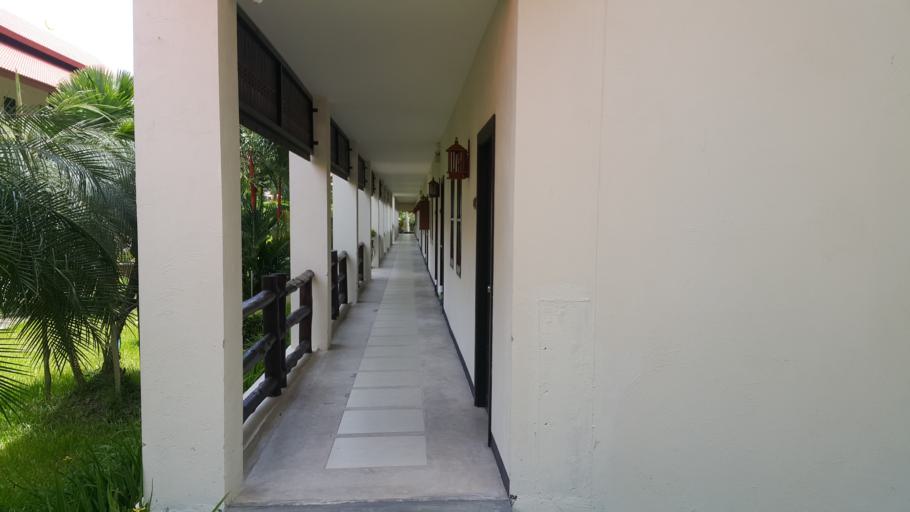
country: TH
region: Chiang Mai
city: San Sai
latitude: 18.8586
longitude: 99.0989
